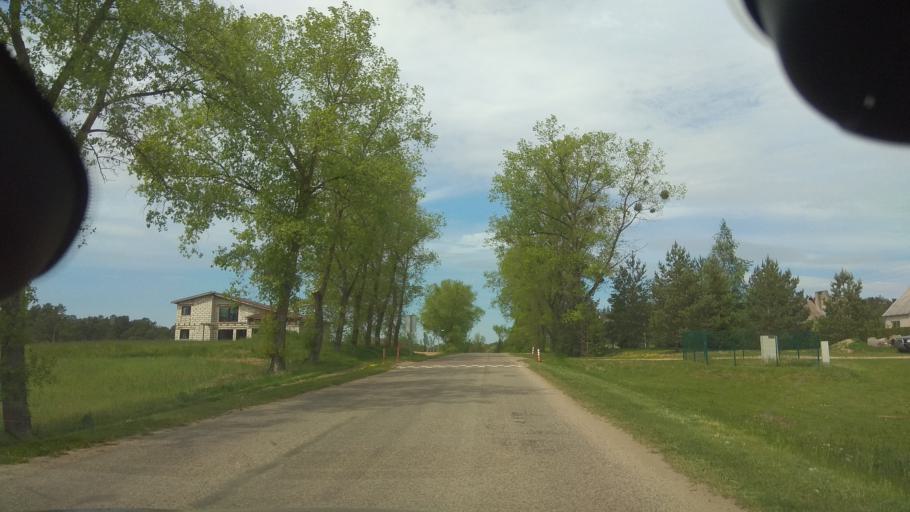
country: LT
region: Vilnius County
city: Ukmerge
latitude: 55.1430
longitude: 24.5870
